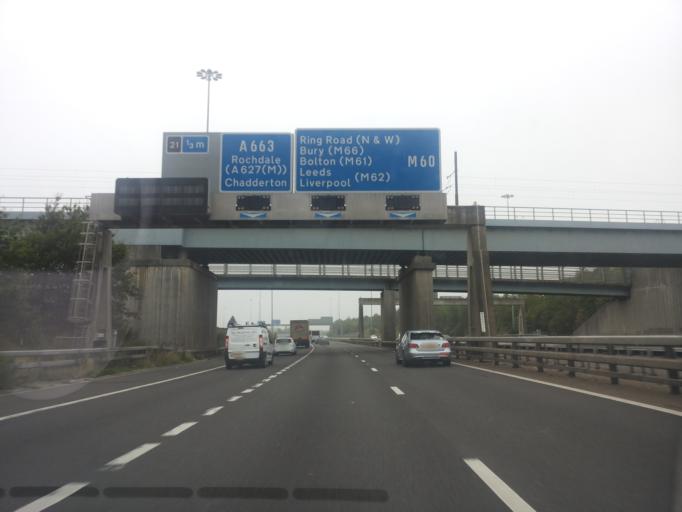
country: GB
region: England
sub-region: Manchester
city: Failsworth
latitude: 53.5208
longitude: -2.1456
